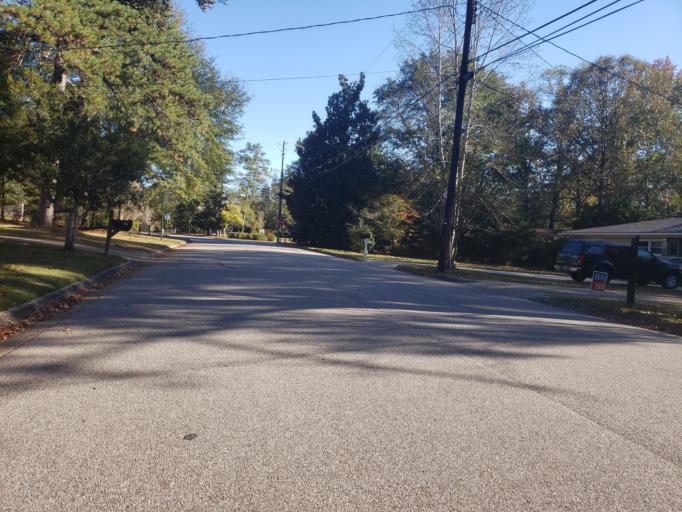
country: US
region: Alabama
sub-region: Lee County
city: Auburn
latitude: 32.5896
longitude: -85.4654
